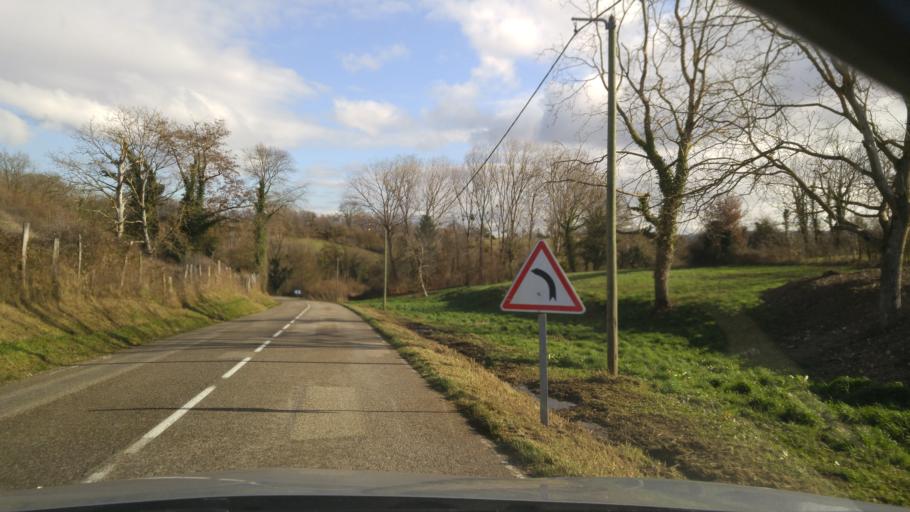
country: FR
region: Rhone-Alpes
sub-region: Departement de l'Isere
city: Roche
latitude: 45.5932
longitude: 5.1633
